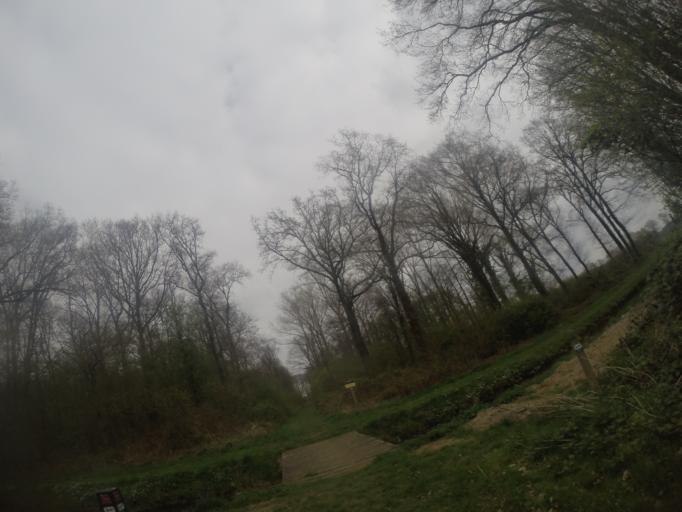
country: NL
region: Gelderland
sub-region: Gemeente Zutphen
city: Leesten
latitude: 52.1206
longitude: 6.2667
